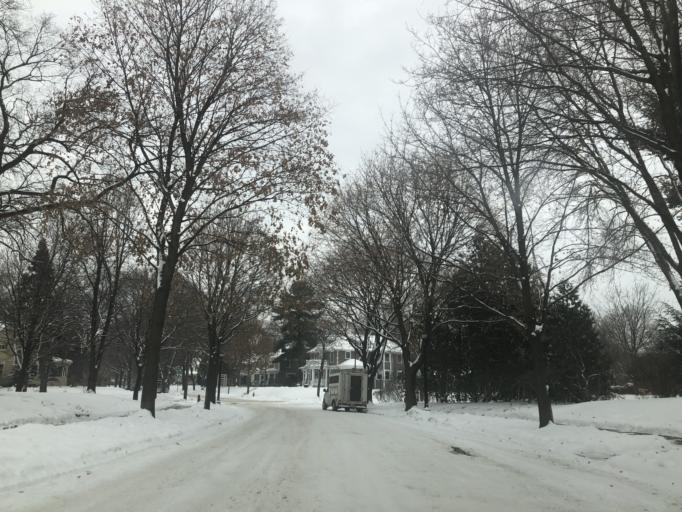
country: US
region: Minnesota
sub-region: Hennepin County
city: Richfield
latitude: 44.9202
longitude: -93.2957
